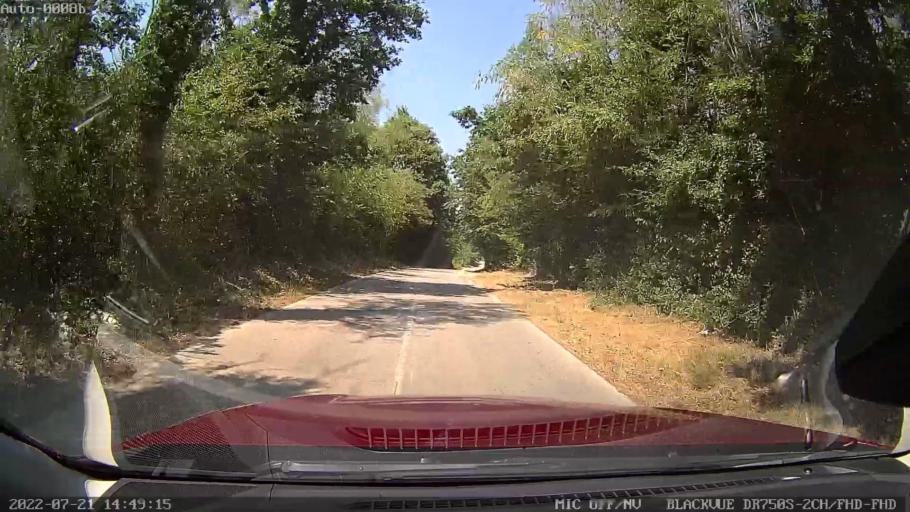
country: HR
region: Istarska
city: Pazin
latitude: 45.1504
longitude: 13.9091
